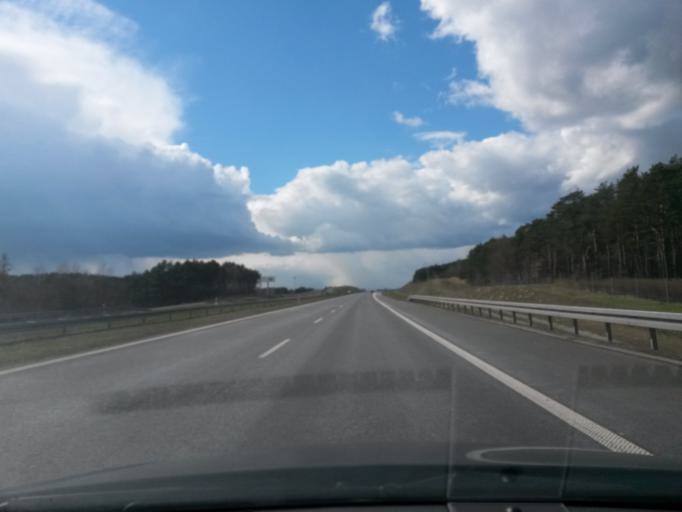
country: PL
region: Greater Poland Voivodeship
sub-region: Powiat kolski
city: Koscielec
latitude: 52.1423
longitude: 18.5314
